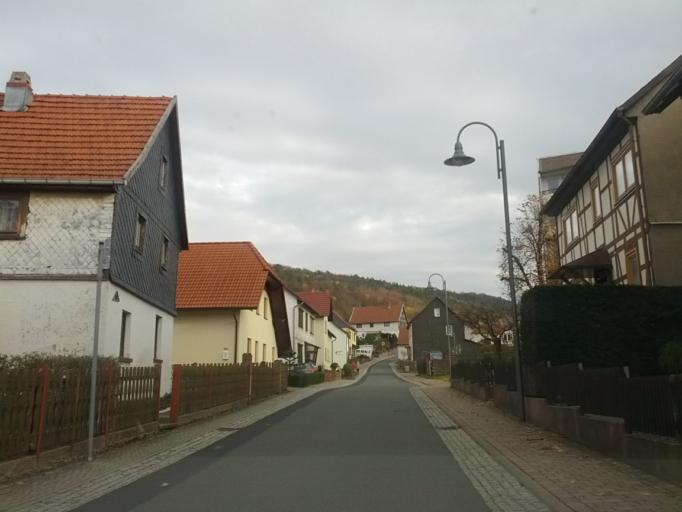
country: DE
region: Thuringia
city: Seebach
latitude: 50.9132
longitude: 10.4282
